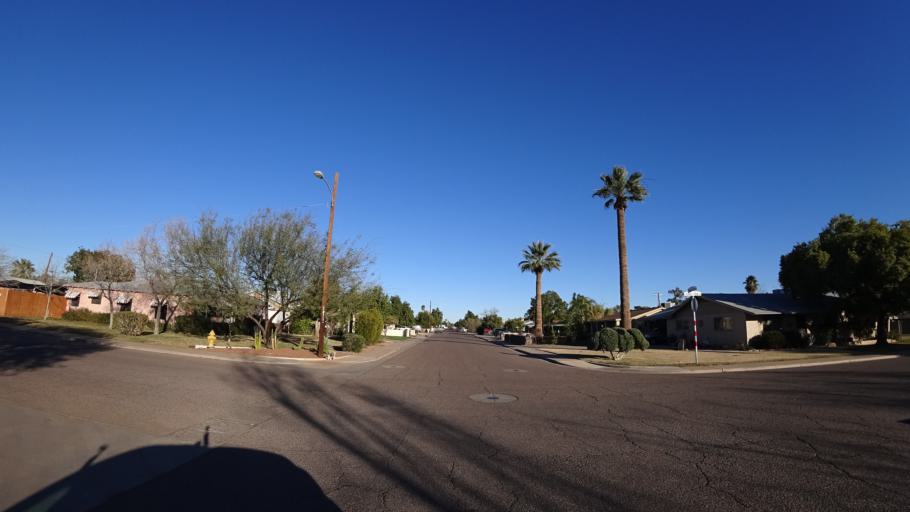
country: US
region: Arizona
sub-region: Maricopa County
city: Phoenix
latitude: 33.4902
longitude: -112.0543
